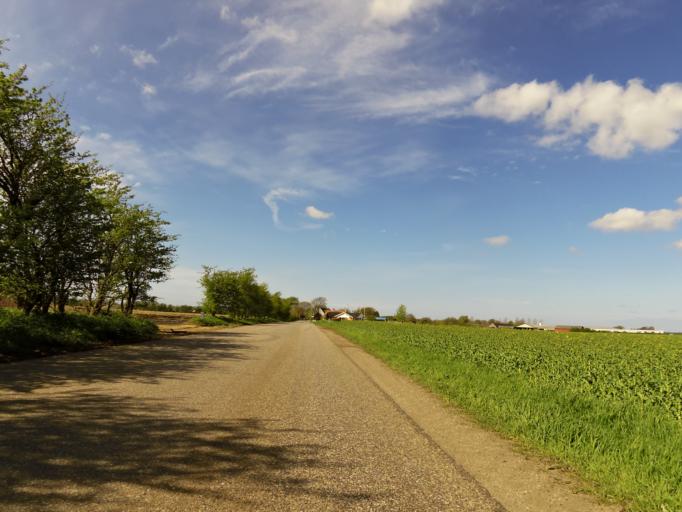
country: DK
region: Central Jutland
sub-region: Skive Kommune
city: Skive
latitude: 56.4656
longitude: 8.9724
